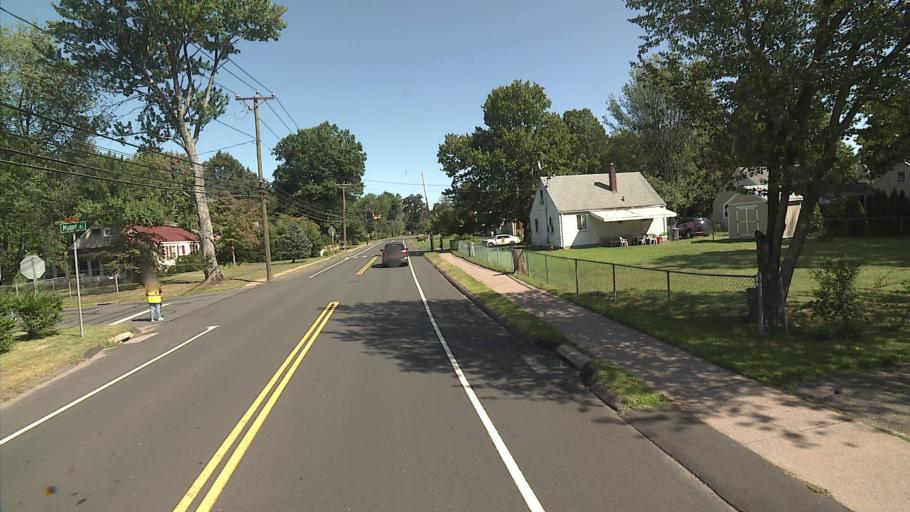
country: US
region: Connecticut
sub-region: Hartford County
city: Windsor
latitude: 41.8400
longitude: -72.6571
